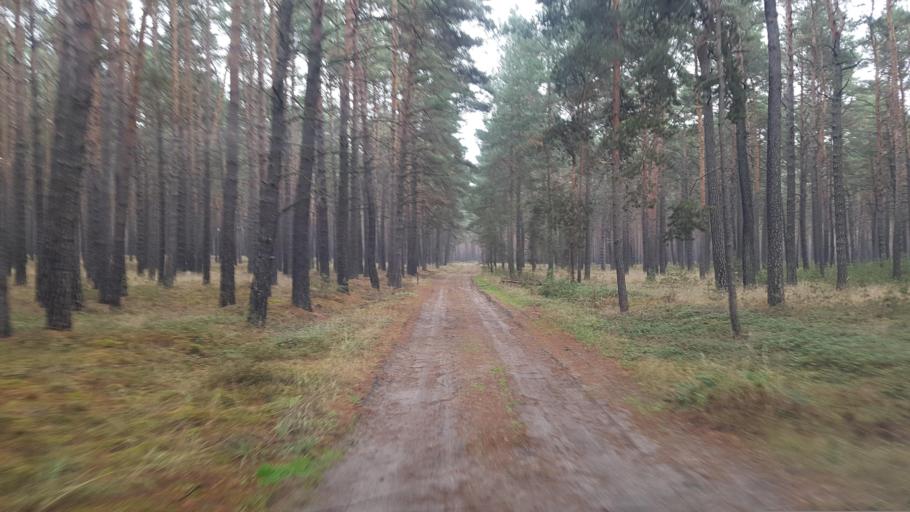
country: DE
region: Brandenburg
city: Sallgast
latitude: 51.6512
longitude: 13.8217
